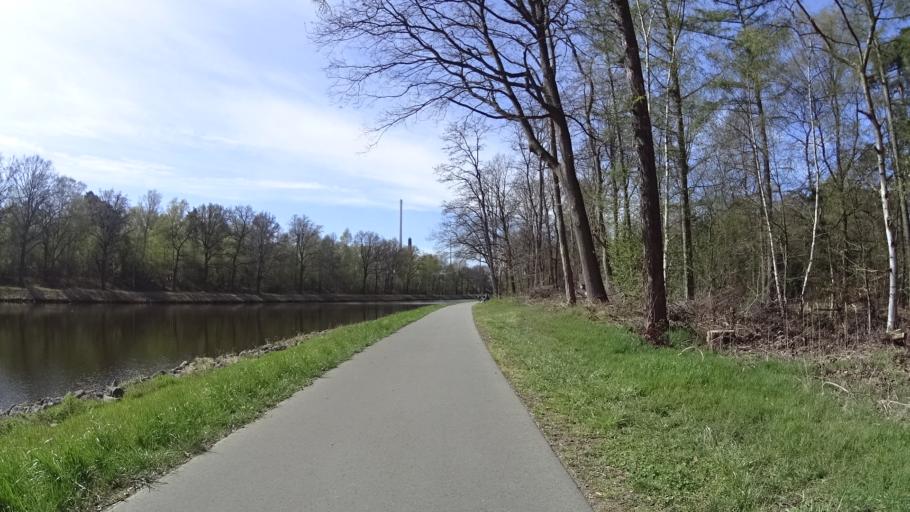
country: DE
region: Lower Saxony
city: Lingen
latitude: 52.5689
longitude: 7.3084
